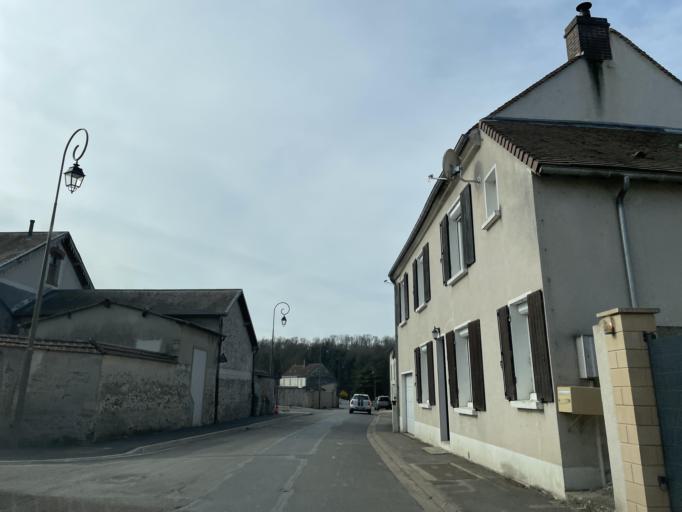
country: FR
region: Ile-de-France
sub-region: Departement de Seine-et-Marne
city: Chailly-en-Brie
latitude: 48.7414
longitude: 3.1282
